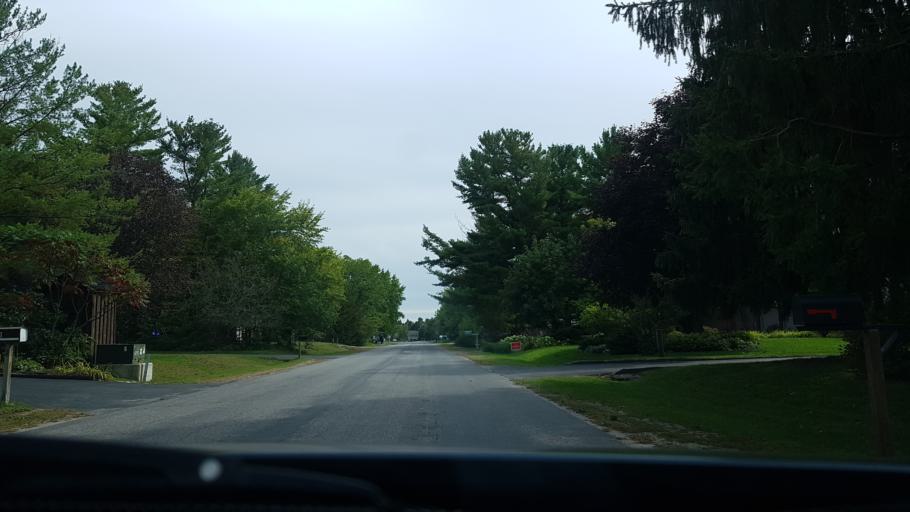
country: CA
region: Ontario
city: Barrie
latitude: 44.4826
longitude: -79.8193
